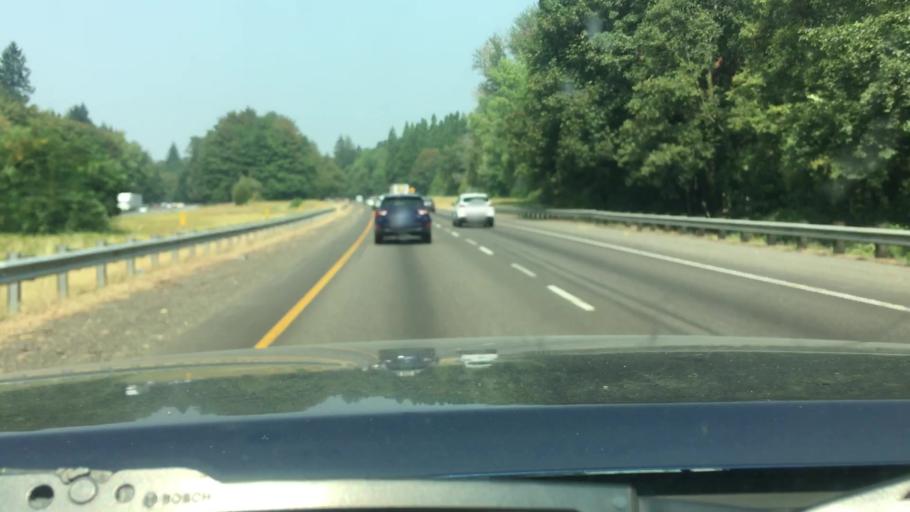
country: US
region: Oregon
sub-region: Clackamas County
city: Stafford
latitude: 45.3610
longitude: -122.6689
